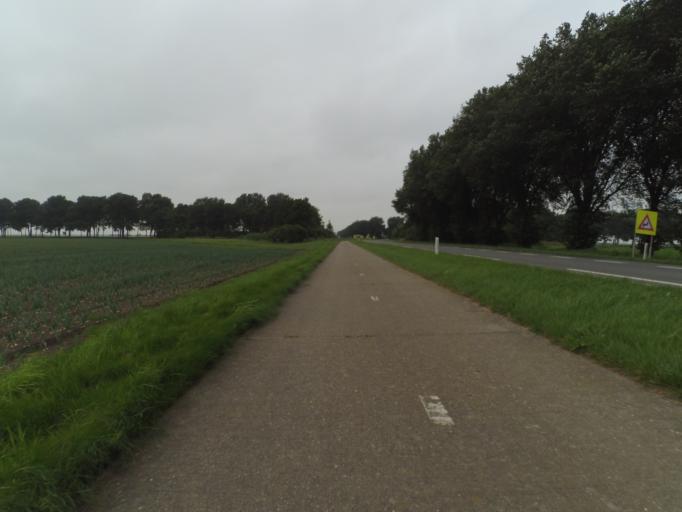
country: NL
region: Flevoland
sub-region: Gemeente Zeewolde
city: Zeewolde
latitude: 52.3872
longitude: 5.4422
